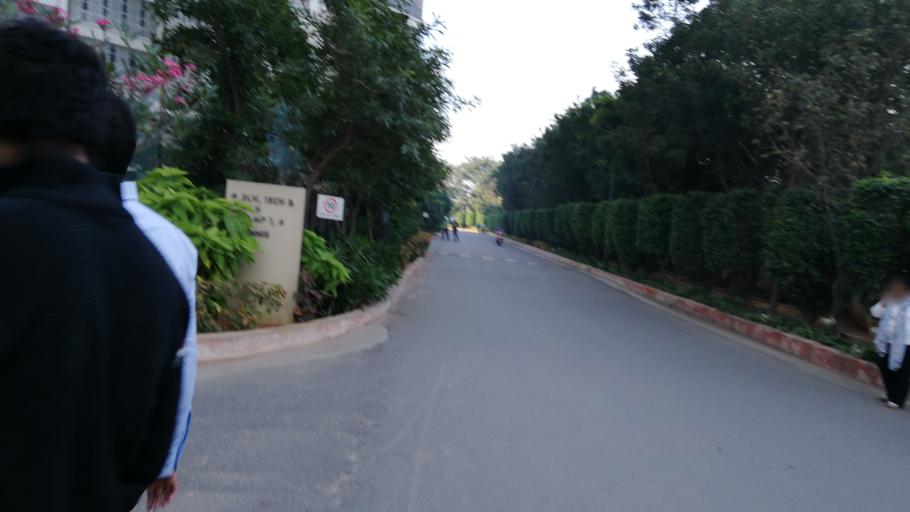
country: IN
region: Telangana
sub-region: Rangareddi
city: Kukatpalli
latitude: 17.4108
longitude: 78.3750
